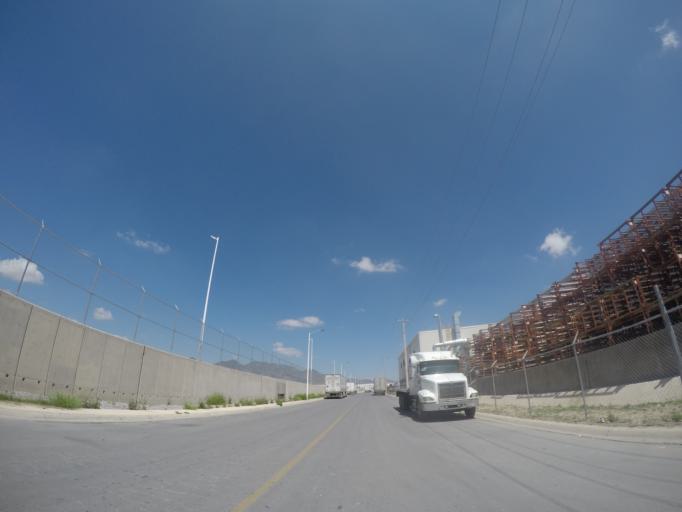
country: MX
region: San Luis Potosi
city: La Pila
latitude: 21.9739
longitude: -100.8776
